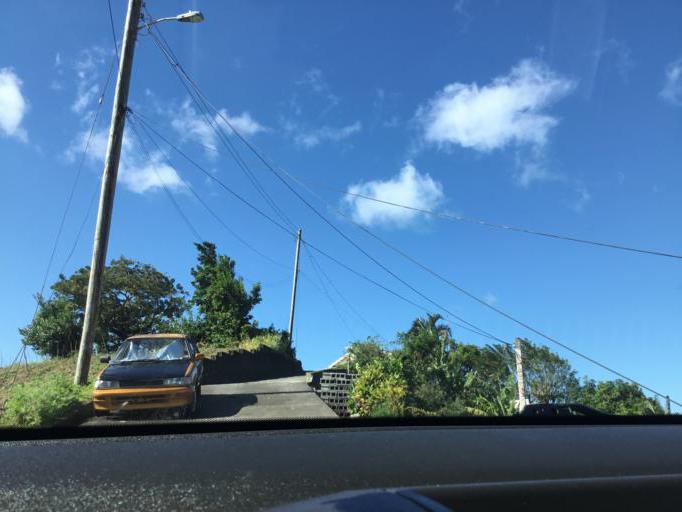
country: VC
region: Saint David
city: Chateaubelair
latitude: 13.2723
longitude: -61.2392
